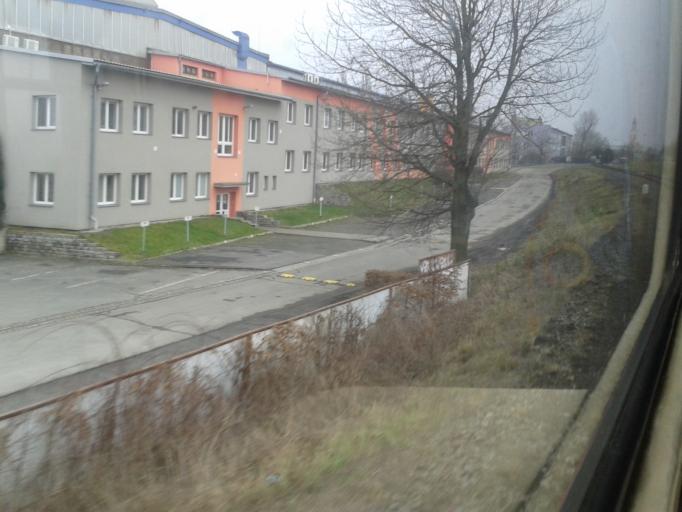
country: CZ
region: Olomoucky
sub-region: Okres Olomouc
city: Olomouc
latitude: 49.6106
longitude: 17.2268
